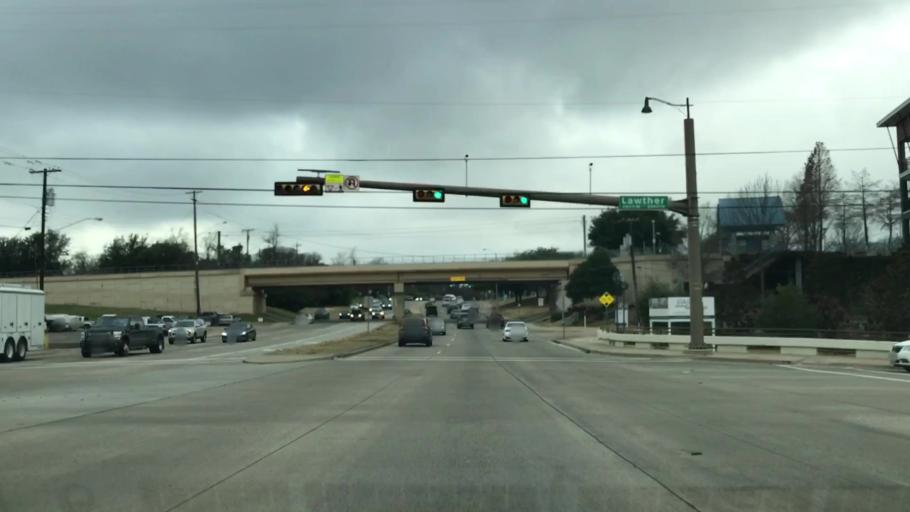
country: US
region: Texas
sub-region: Dallas County
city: Highland Park
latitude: 32.8556
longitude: -96.7315
